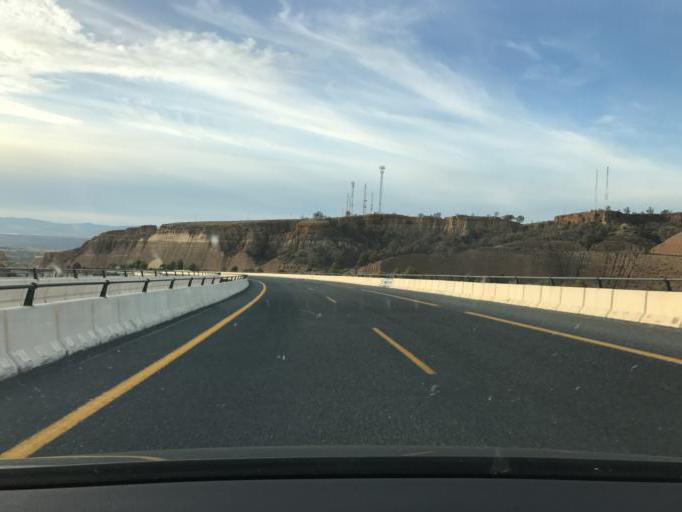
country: ES
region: Andalusia
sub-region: Provincia de Granada
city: Guadix
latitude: 37.3198
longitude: -3.1152
